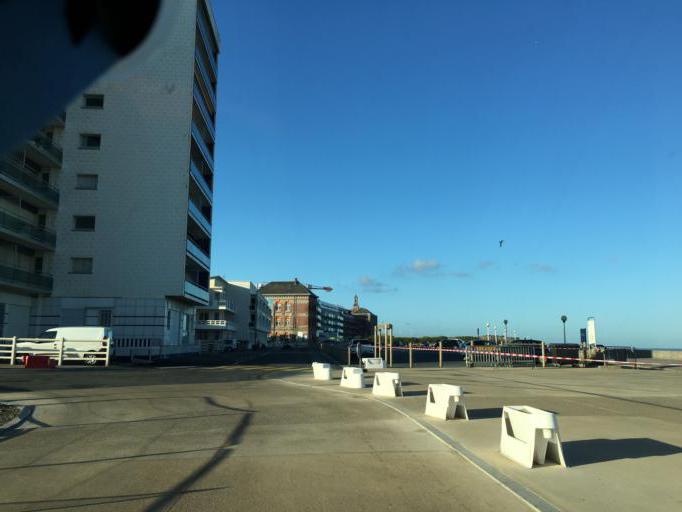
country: FR
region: Nord-Pas-de-Calais
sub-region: Departement du Pas-de-Calais
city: Berck-Plage
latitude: 50.4045
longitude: 1.5590
